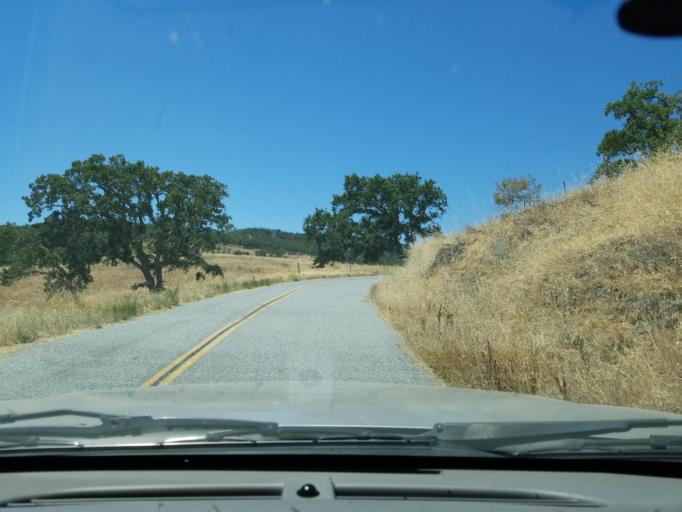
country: US
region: California
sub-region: Monterey County
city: Gonzales
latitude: 36.3959
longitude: -121.5748
